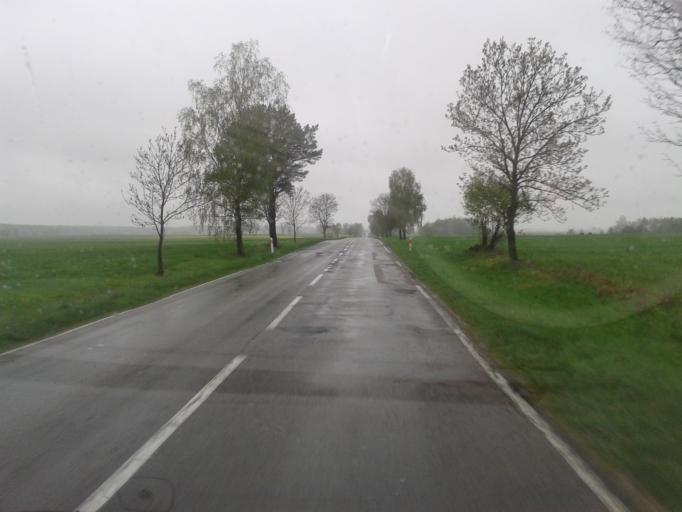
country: PL
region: Subcarpathian Voivodeship
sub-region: Powiat lubaczowski
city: Nowe Siolo
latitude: 50.2903
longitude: 23.1917
